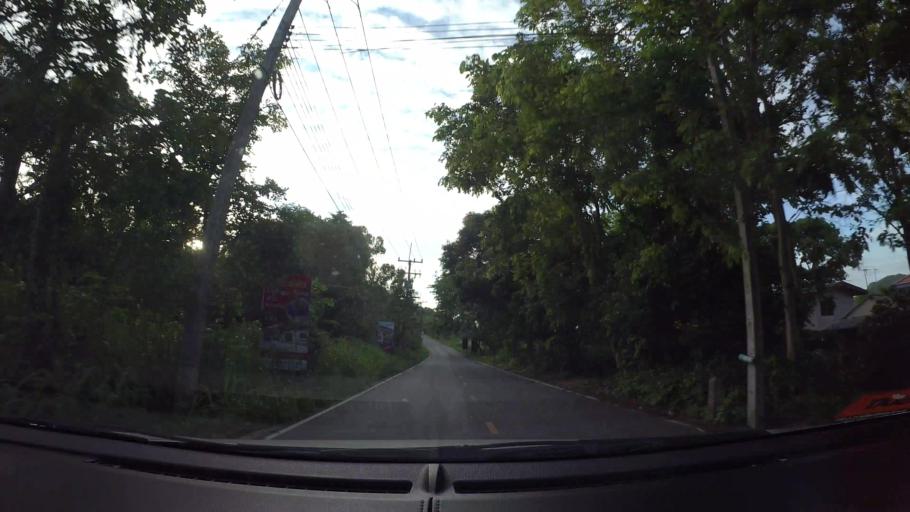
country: TH
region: Chon Buri
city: Sattahip
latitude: 12.7426
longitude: 100.9355
